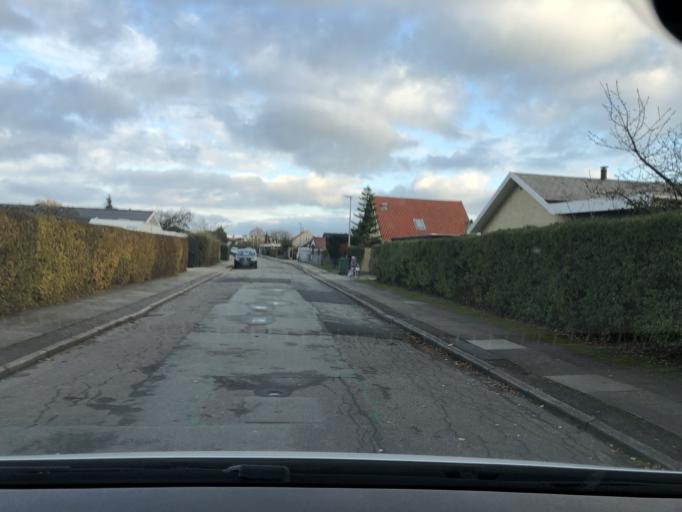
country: DK
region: Capital Region
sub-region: Tarnby Kommune
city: Tarnby
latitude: 55.6209
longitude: 12.5977
